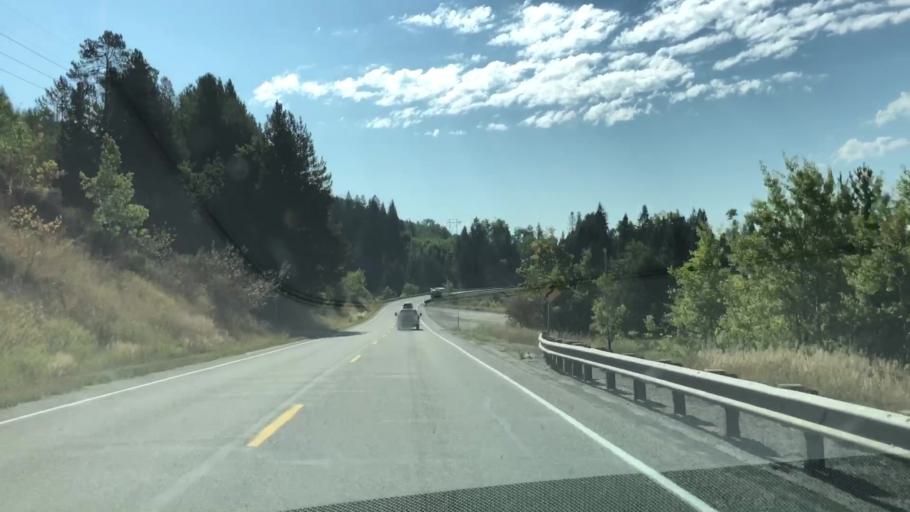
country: US
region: Idaho
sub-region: Teton County
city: Victor
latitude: 43.3016
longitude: -111.1317
